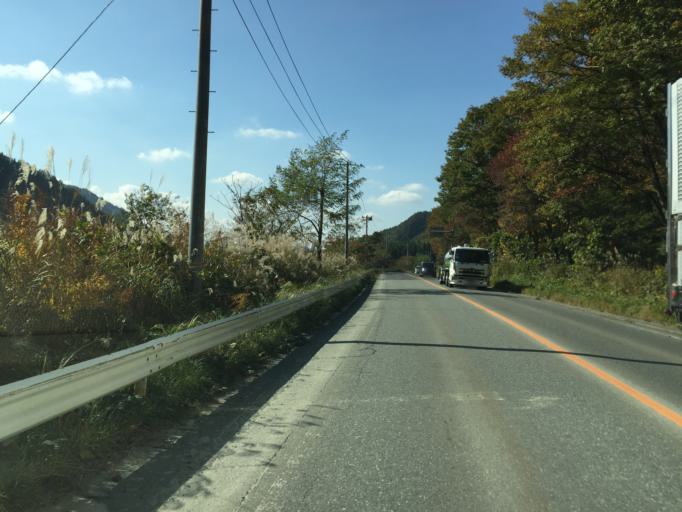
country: JP
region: Yamagata
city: Yonezawa
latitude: 37.8696
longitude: 140.2278
